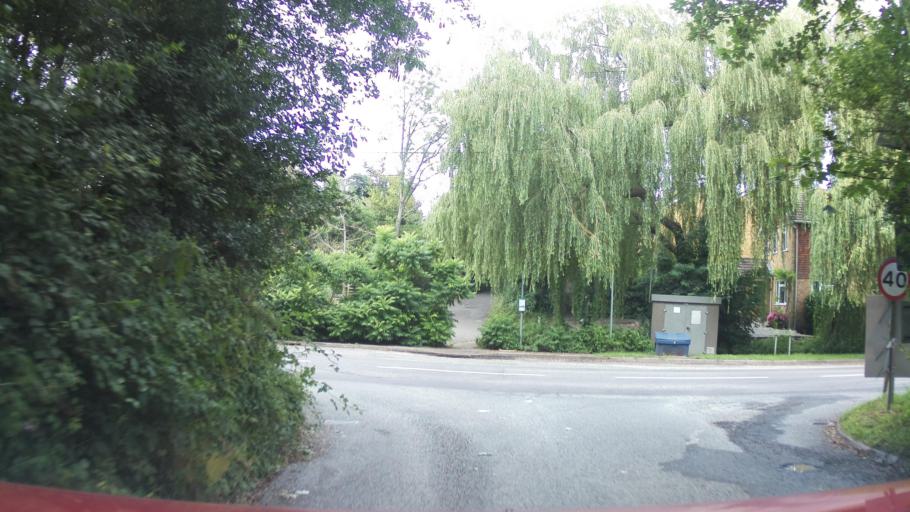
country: GB
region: England
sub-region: Hampshire
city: Colden Common
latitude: 50.9922
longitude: -1.3247
